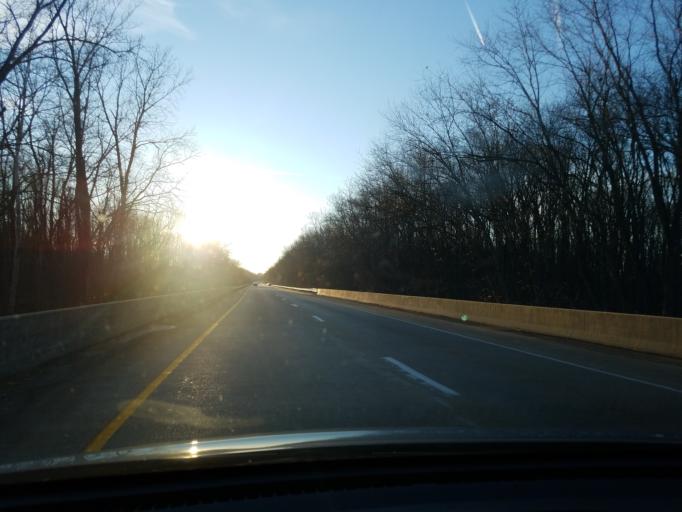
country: US
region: Indiana
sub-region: Warrick County
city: Chandler
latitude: 38.1753
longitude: -87.4164
